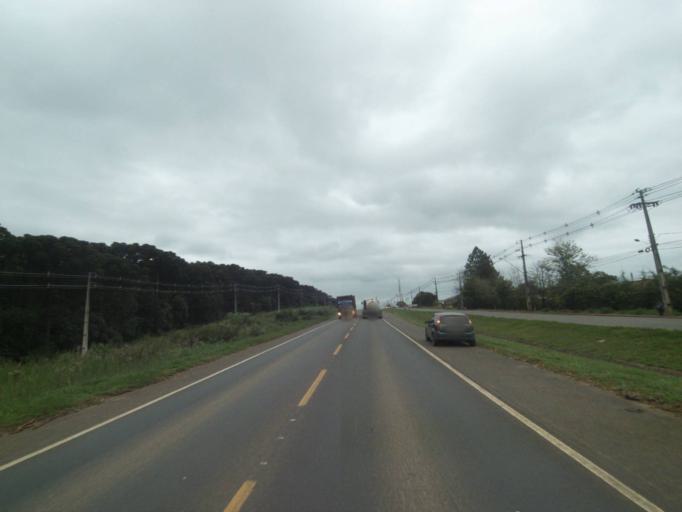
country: BR
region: Parana
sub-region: Telemaco Borba
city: Telemaco Borba
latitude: -24.3725
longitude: -50.6630
